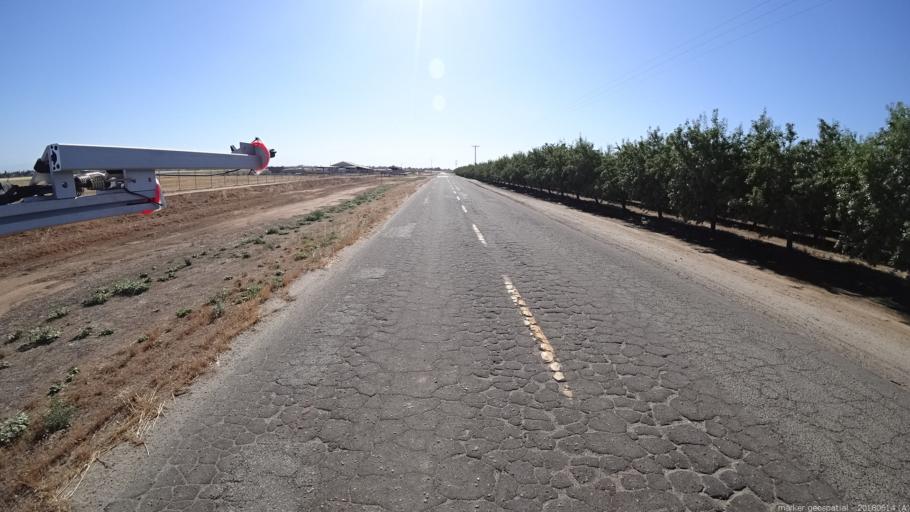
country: US
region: California
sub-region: Madera County
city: Madera
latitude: 36.9819
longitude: -120.1138
